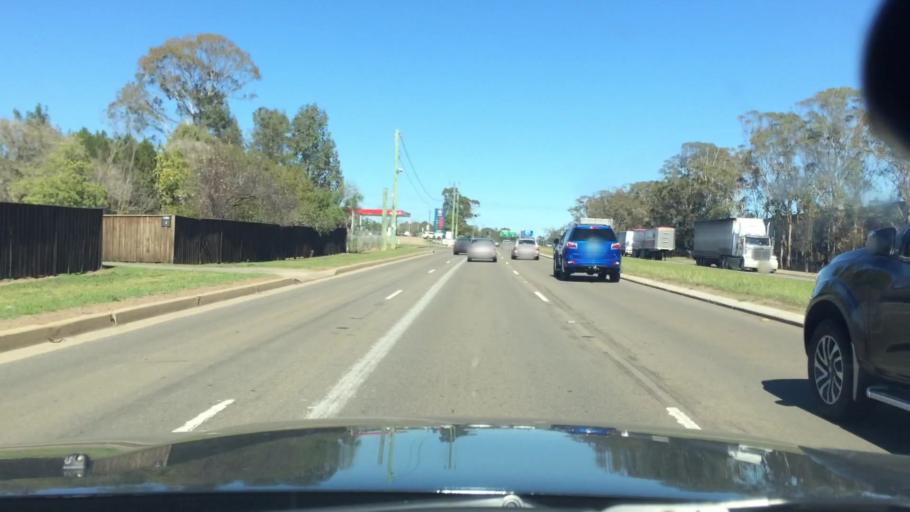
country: AU
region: New South Wales
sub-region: Campbelltown Municipality
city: Glenfield
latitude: -33.9619
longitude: 150.8823
